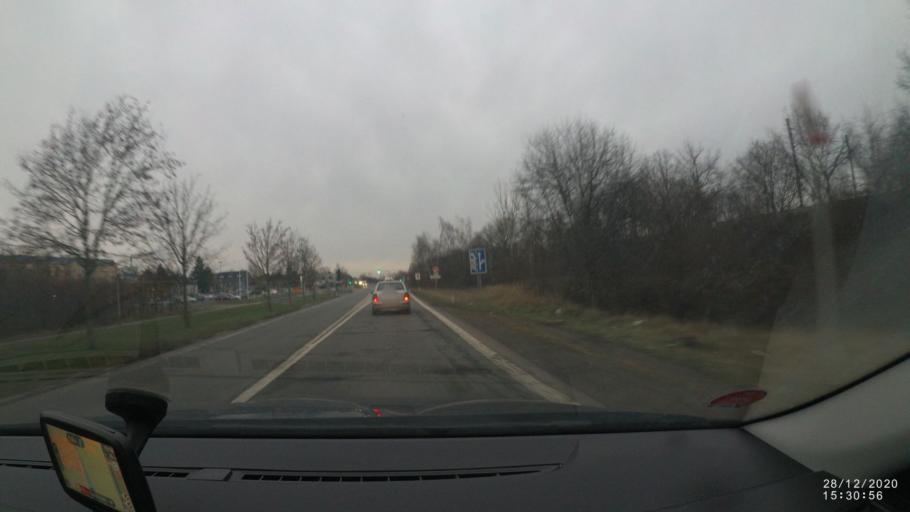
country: CZ
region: Praha
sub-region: Praha 14
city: Dolni Pocernice
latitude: 50.0874
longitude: 14.5656
